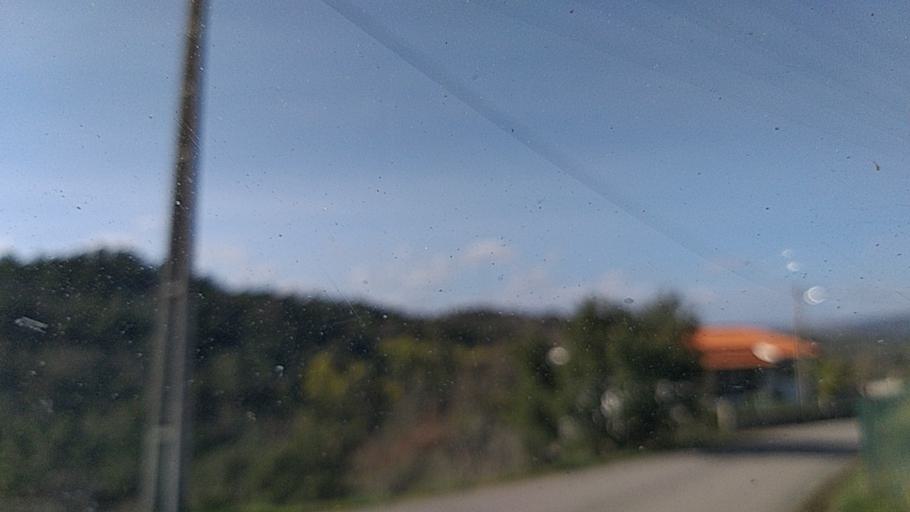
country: PT
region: Guarda
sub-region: Celorico da Beira
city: Celorico da Beira
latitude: 40.6341
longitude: -7.3976
